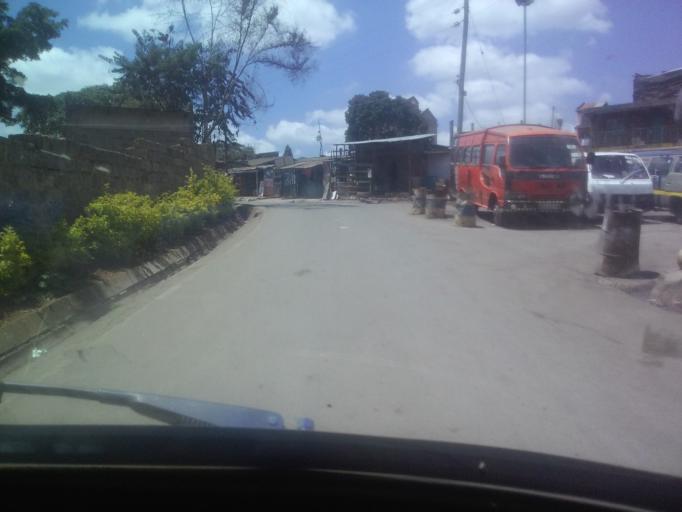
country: KE
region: Nairobi Area
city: Nairobi
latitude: -1.3090
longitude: 36.7760
